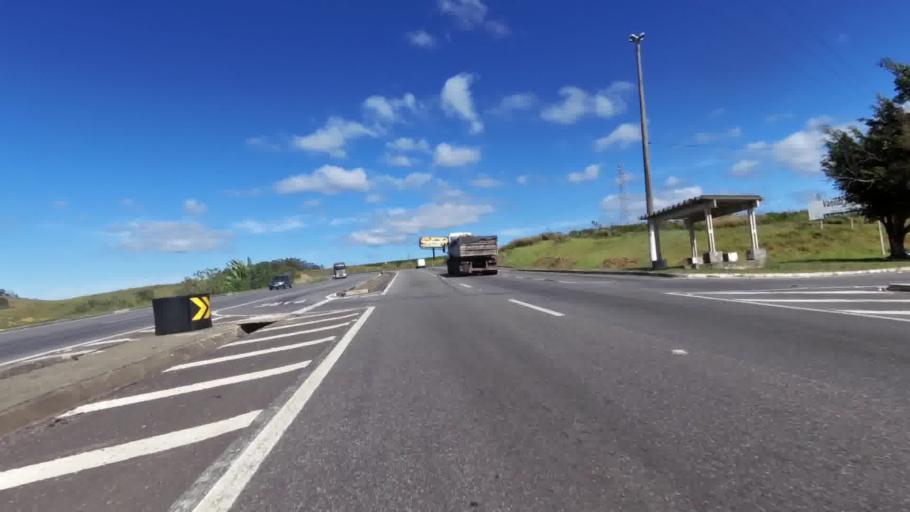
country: BR
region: Espirito Santo
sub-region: Alfredo Chaves
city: Alfredo Chaves
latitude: -20.6904
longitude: -40.7014
